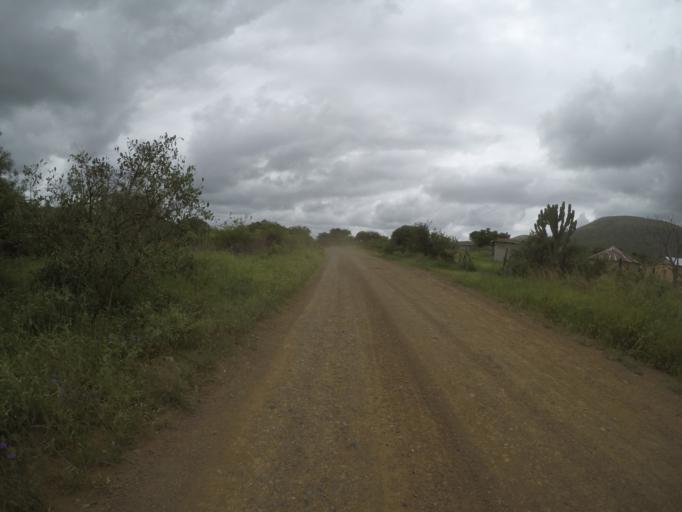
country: ZA
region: KwaZulu-Natal
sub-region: uThungulu District Municipality
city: Empangeni
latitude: -28.5616
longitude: 31.8744
